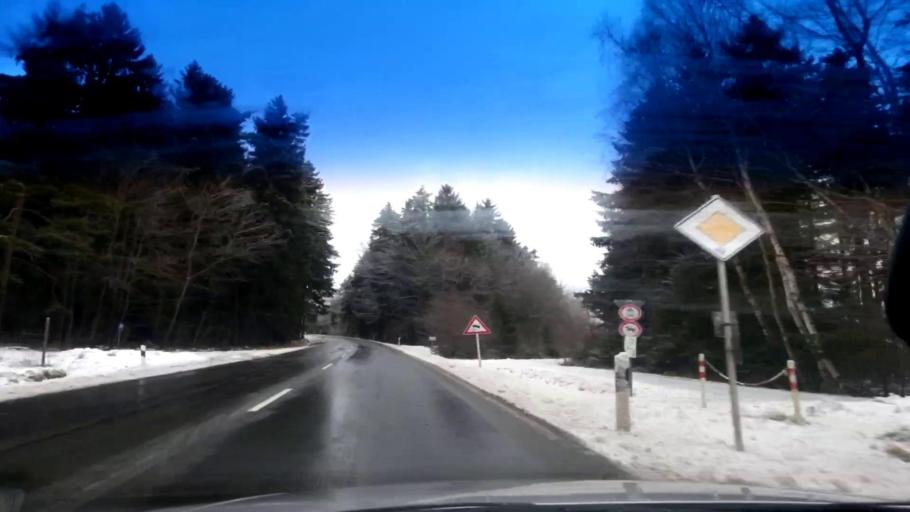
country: DE
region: Bavaria
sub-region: Upper Franconia
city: Kirchenlamitz
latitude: 50.1350
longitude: 11.9267
